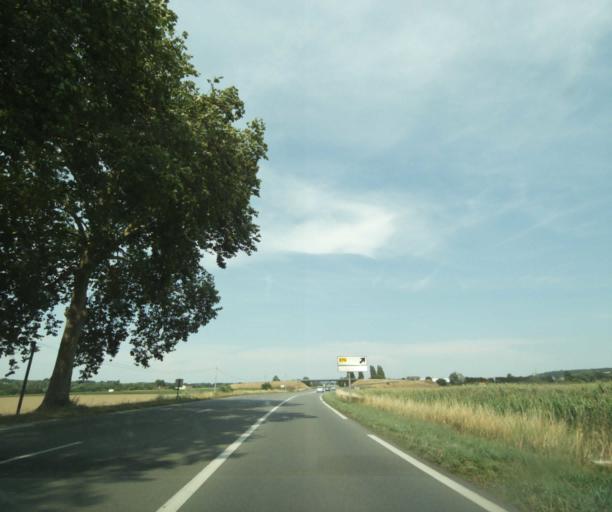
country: FR
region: Poitou-Charentes
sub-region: Departement de la Vienne
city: Dange-Saint-Romain
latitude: 46.8954
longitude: 0.5701
